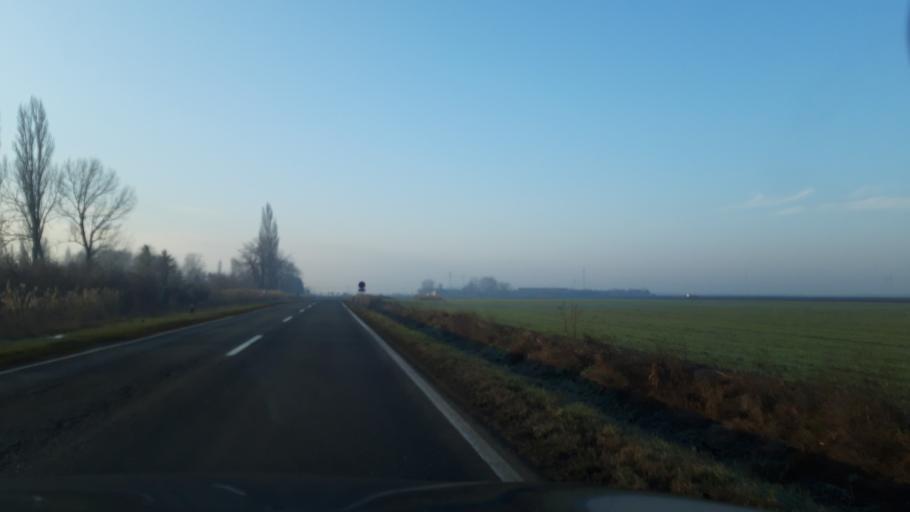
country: RS
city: Jarak
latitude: 44.9460
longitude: 19.7967
